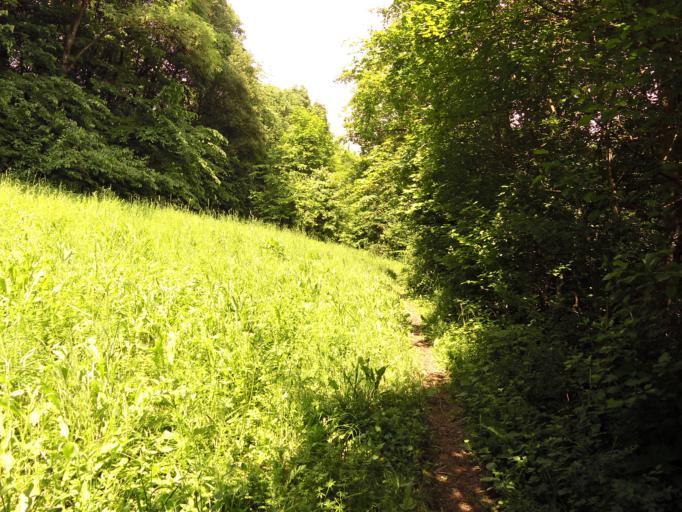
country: DE
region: Bavaria
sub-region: Regierungsbezirk Unterfranken
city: Hochberg
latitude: 49.7940
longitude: 9.8843
